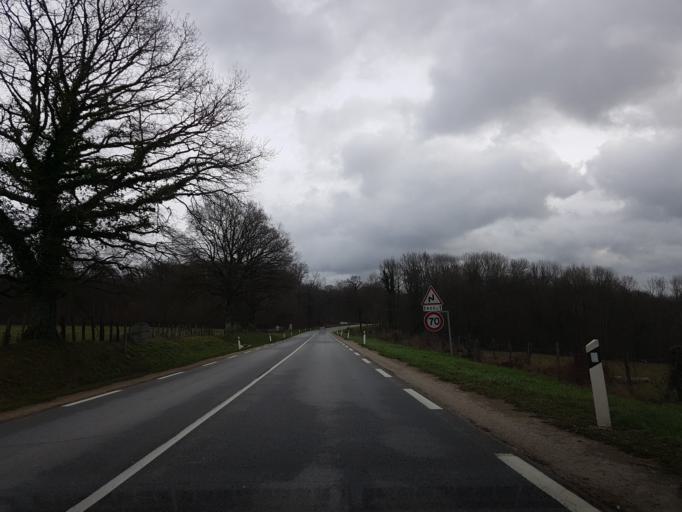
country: FR
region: Champagne-Ardenne
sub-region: Departement de la Haute-Marne
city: Fayl-Billot
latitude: 47.8079
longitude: 5.5541
